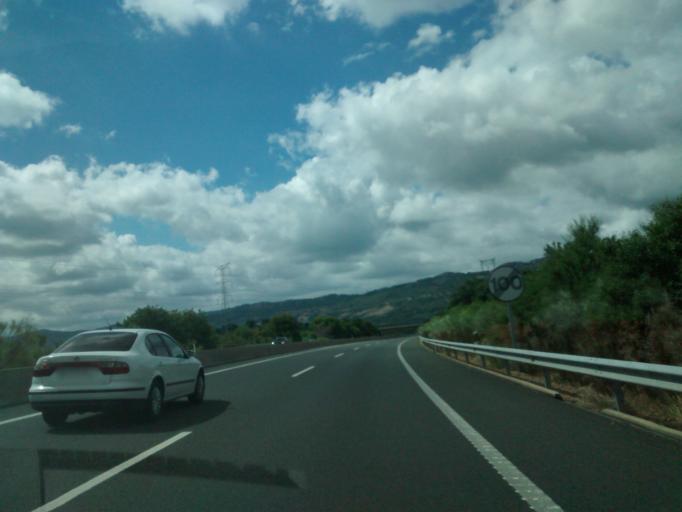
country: ES
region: Extremadura
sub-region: Provincia de Caceres
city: Casas de Miravete
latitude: 39.7417
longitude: -5.7249
